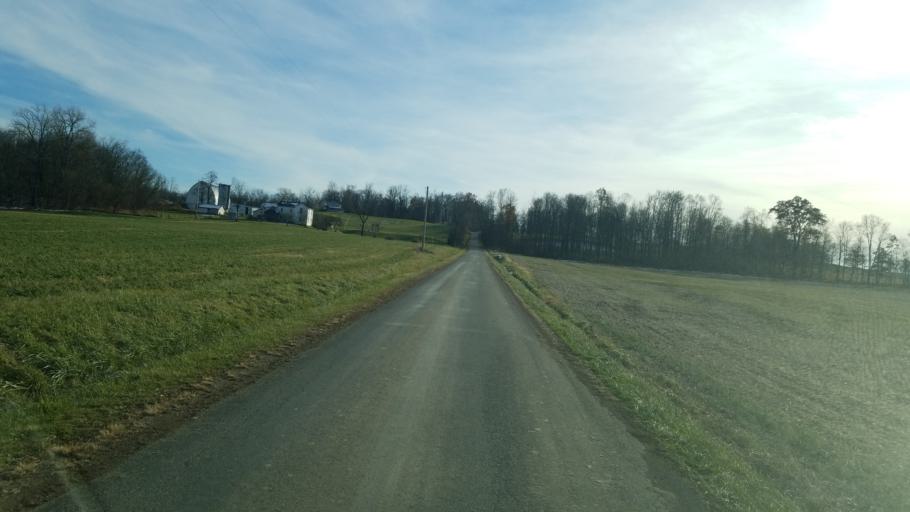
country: US
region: Ohio
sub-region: Ashland County
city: Ashland
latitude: 40.8160
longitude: -82.2277
